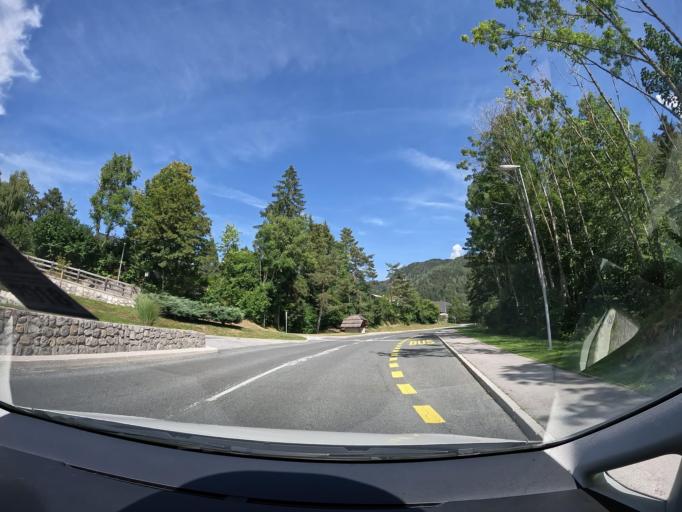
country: AT
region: Carinthia
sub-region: Politischer Bezirk Klagenfurt Land
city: Moosburg
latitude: 46.6603
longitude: 14.1306
